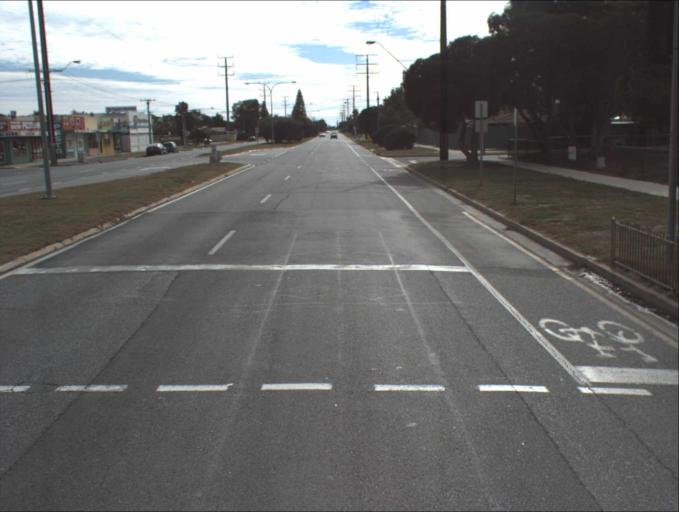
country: AU
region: South Australia
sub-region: Port Adelaide Enfield
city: Birkenhead
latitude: -34.8049
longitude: 138.5014
